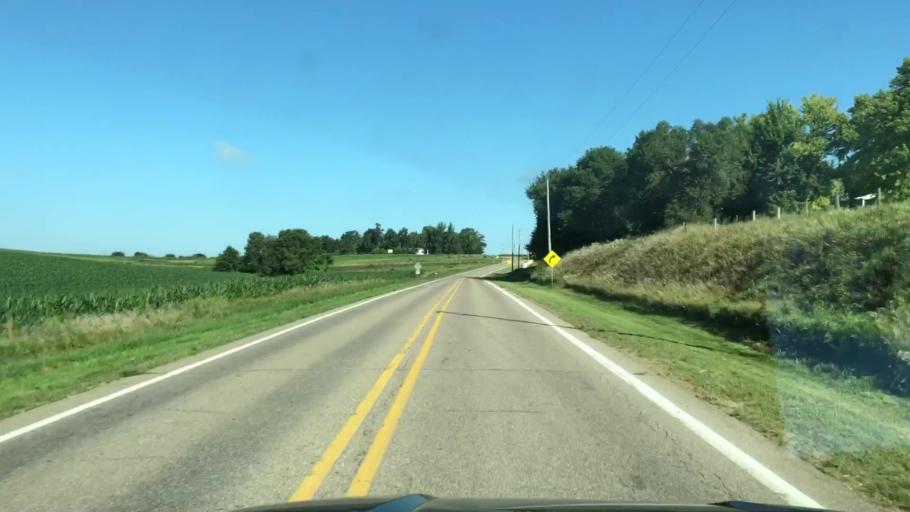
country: US
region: Iowa
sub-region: Woodbury County
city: Sergeant Bluff
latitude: 42.4223
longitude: -96.2746
